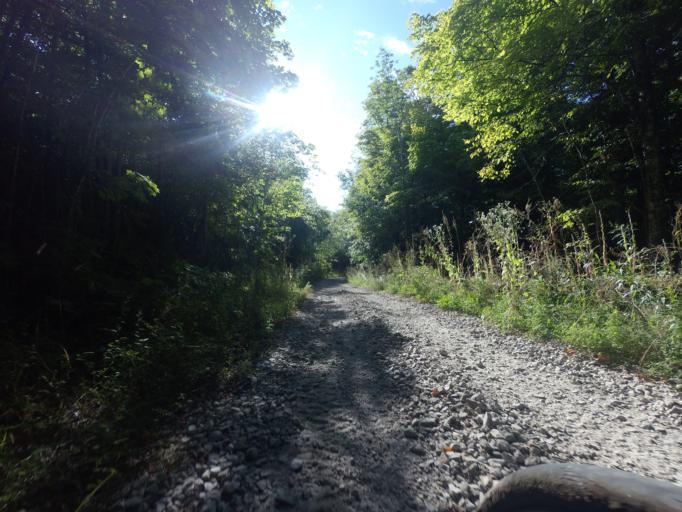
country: CA
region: Ontario
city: Arnprior
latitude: 45.1969
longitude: -76.5230
